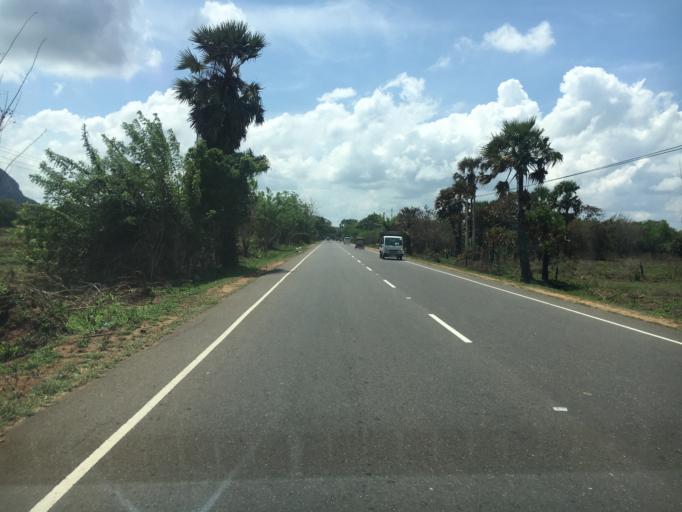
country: LK
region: North Central
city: Anuradhapura
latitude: 8.2789
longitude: 80.4964
